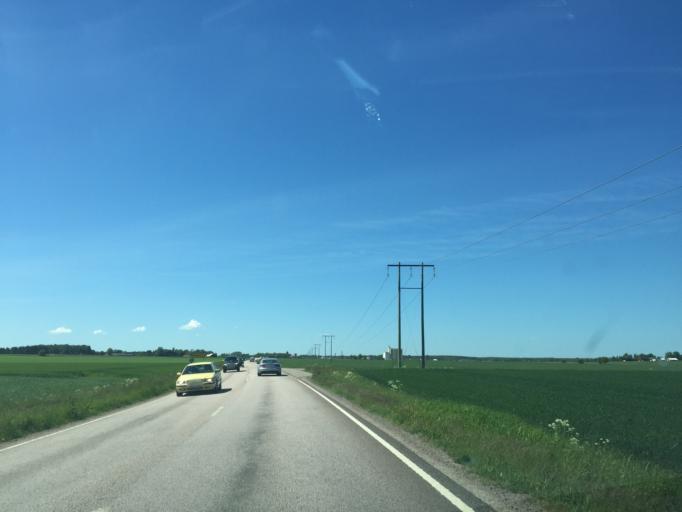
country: SE
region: OEstergoetland
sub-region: Mjolby Kommun
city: Mjolby
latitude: 58.3867
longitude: 15.1379
